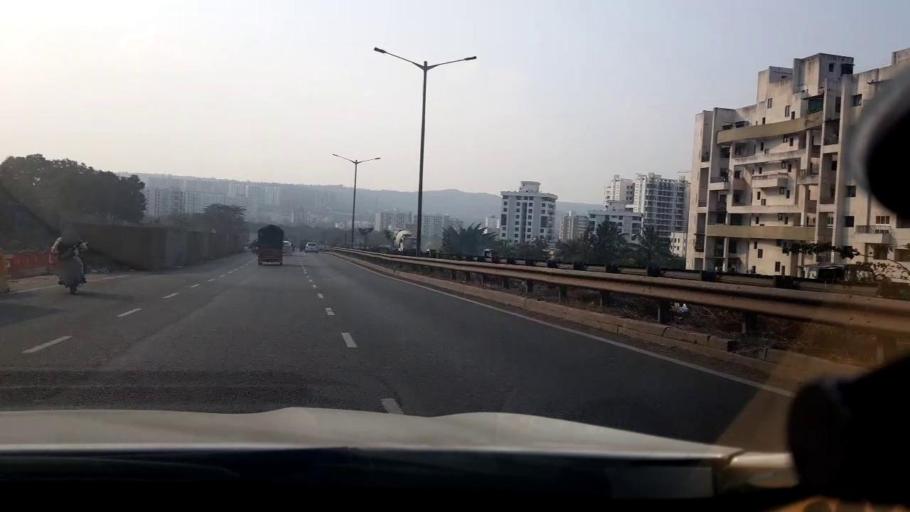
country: IN
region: Maharashtra
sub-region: Pune Division
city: Kharakvasla
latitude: 18.5090
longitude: 73.7777
